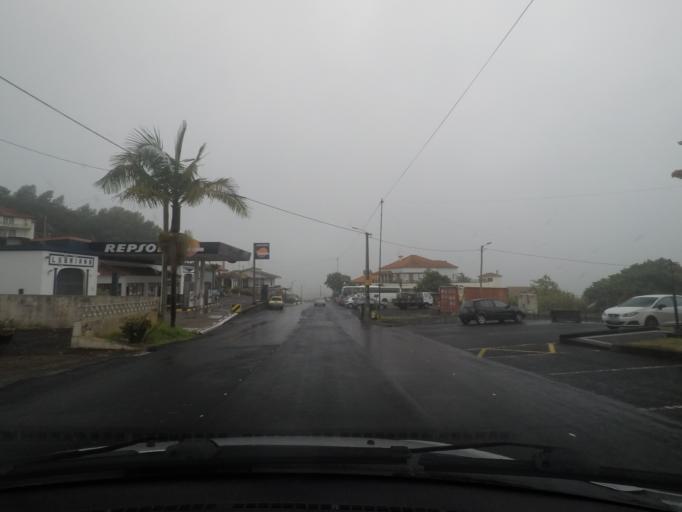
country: PT
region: Madeira
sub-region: Santana
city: Santana
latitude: 32.8014
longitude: -16.8785
